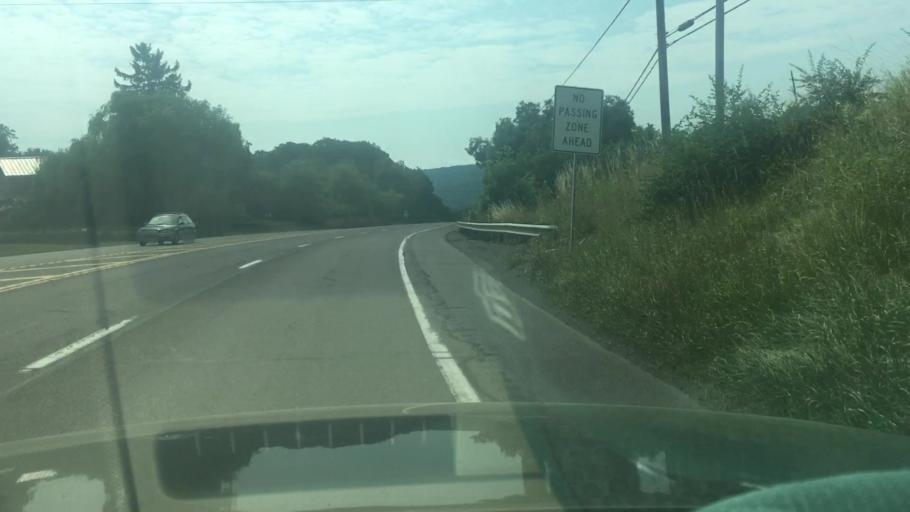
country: US
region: Pennsylvania
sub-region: Northumberland County
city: Elysburg
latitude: 40.8483
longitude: -76.5259
